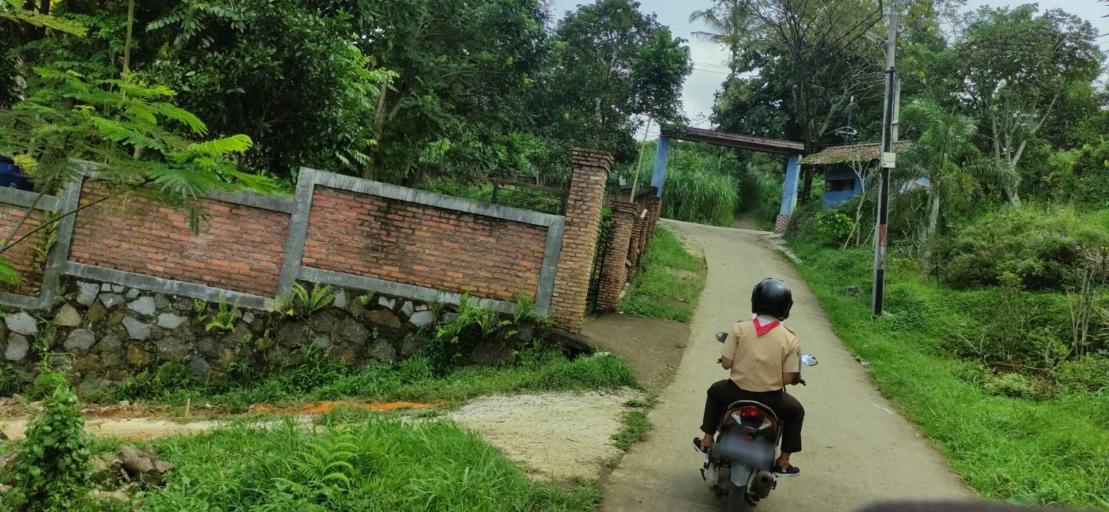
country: ID
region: West Java
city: Caringin
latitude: -6.6420
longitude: 106.8890
